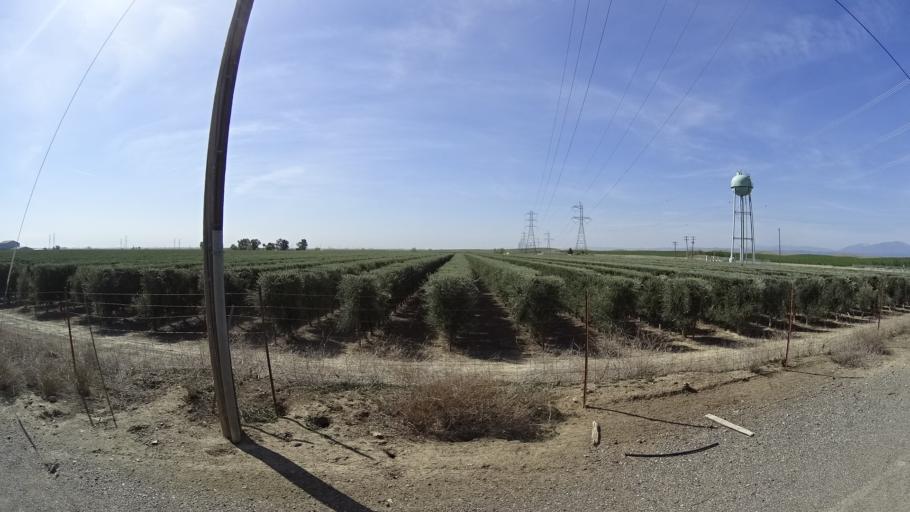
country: US
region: California
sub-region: Glenn County
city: Willows
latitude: 39.6116
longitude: -122.2733
